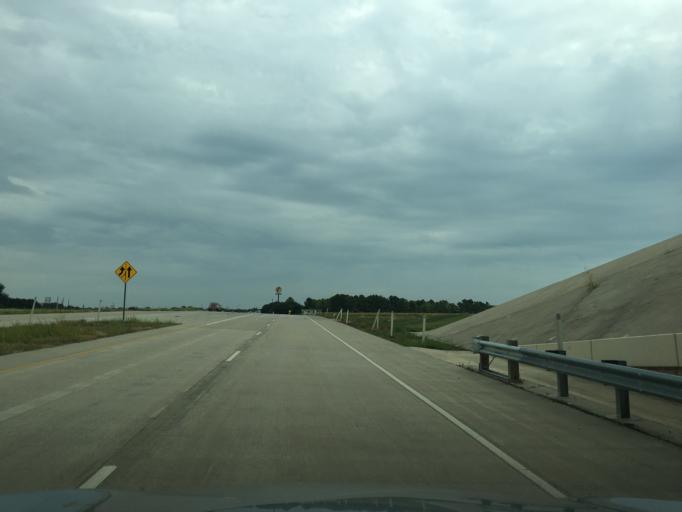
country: US
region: Texas
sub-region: Collin County
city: Melissa
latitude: 33.2651
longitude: -96.5982
